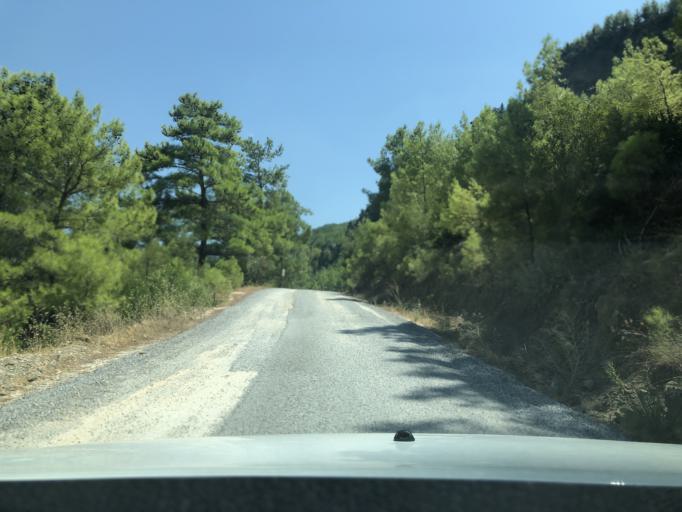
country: TR
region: Antalya
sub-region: Manavgat
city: Manavgat
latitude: 36.9097
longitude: 31.5511
